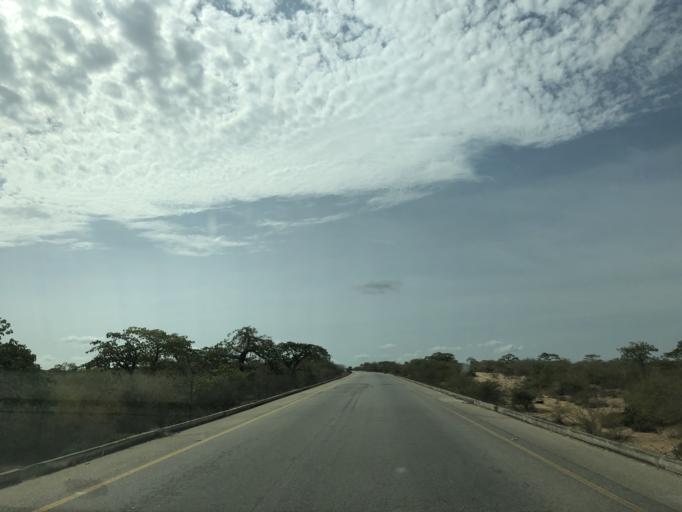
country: AO
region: Benguela
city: Benguela
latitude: -13.0138
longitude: 13.7173
